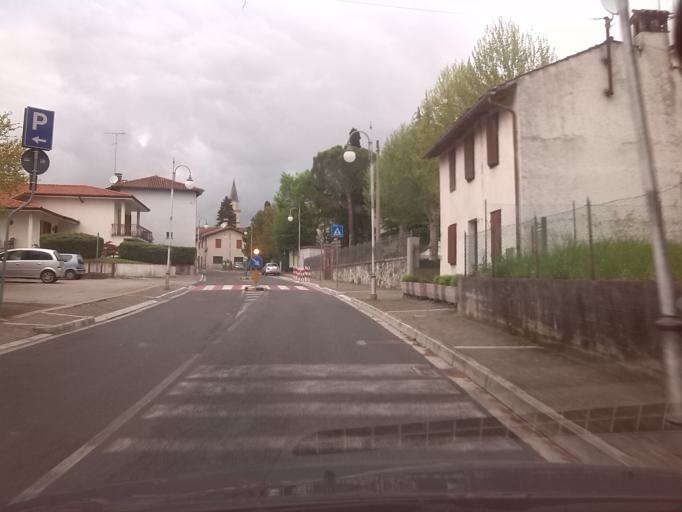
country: IT
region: Friuli Venezia Giulia
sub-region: Provincia di Gorizia
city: Farra d'Isonzo
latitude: 45.9055
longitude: 13.5194
